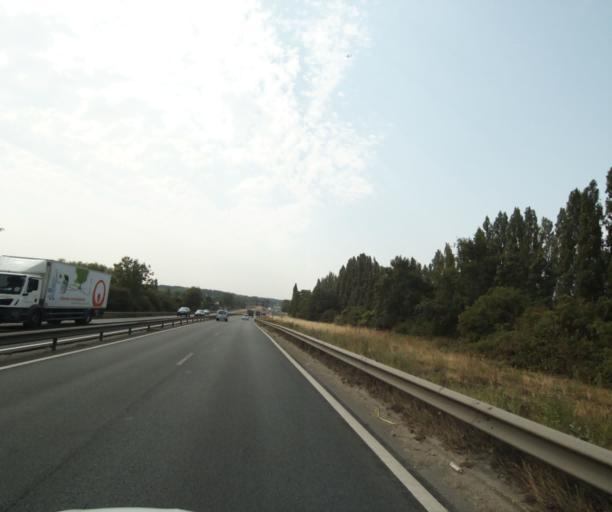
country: FR
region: Ile-de-France
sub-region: Departement des Yvelines
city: Conflans-Sainte-Honorine
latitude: 48.9871
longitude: 2.0836
